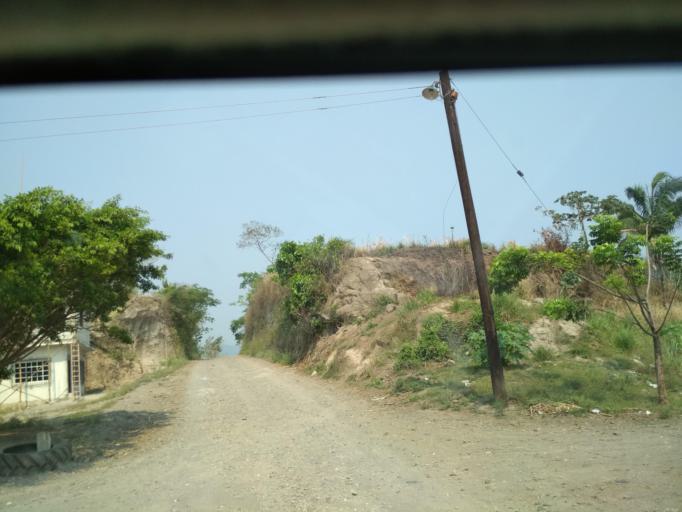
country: MX
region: Oaxaca
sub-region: Acatlan de Perez Figueroa
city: Zona Urbana Ejidal
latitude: 18.5891
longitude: -96.5567
